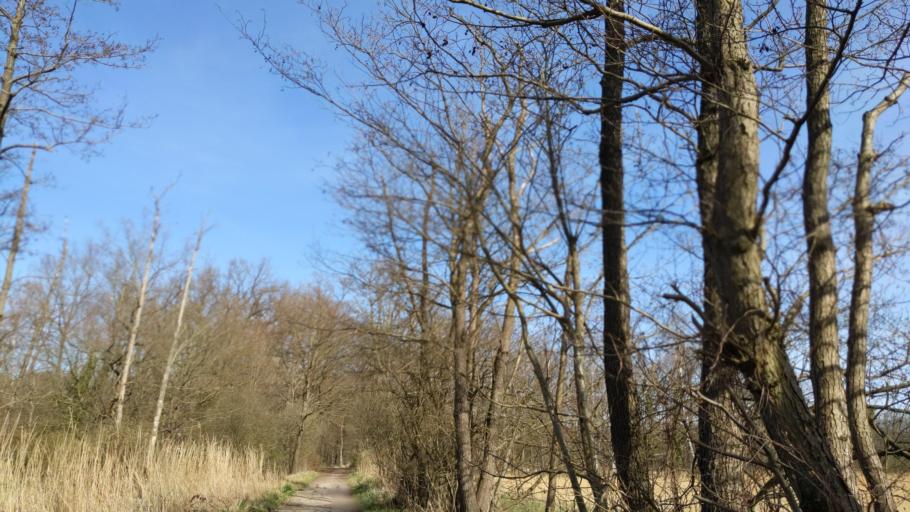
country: DE
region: Schleswig-Holstein
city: Bad Schwartau
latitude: 53.8964
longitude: 10.7242
